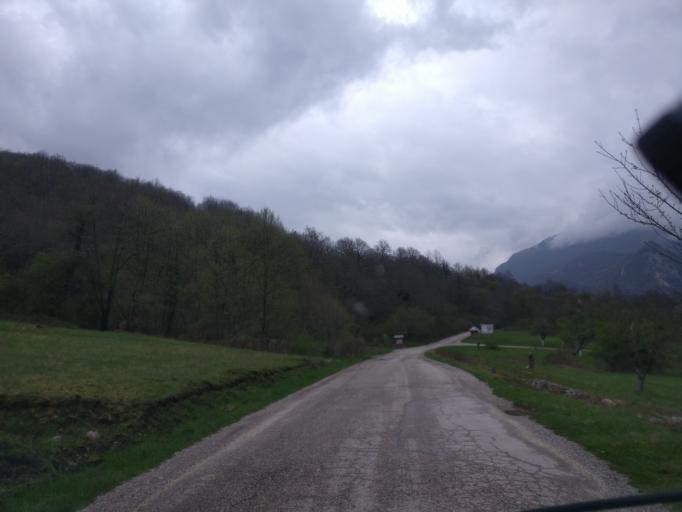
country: BA
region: Republika Srpska
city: Foca
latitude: 43.3532
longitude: 18.8242
